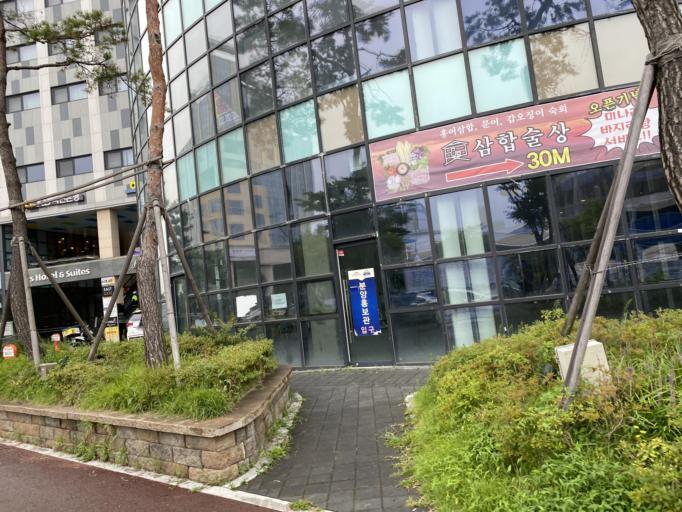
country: KR
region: Incheon
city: Incheon
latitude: 37.4937
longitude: 126.4925
